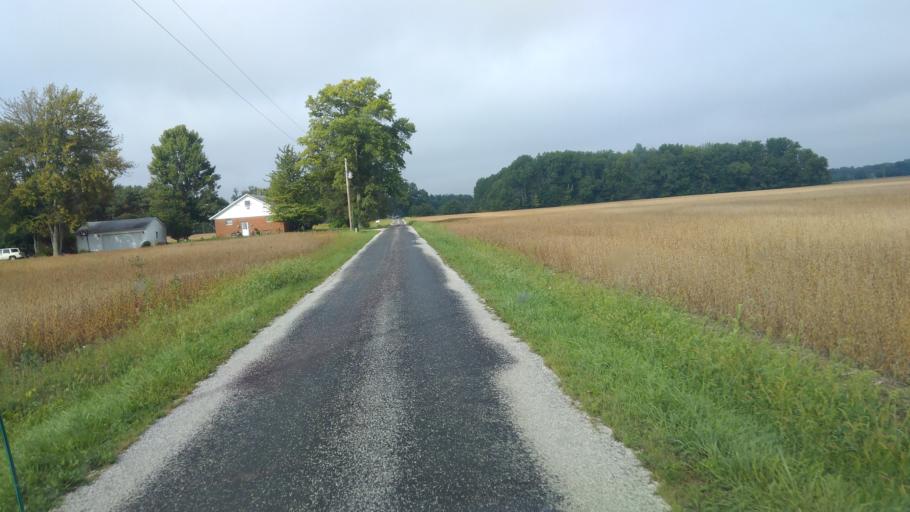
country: US
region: Ohio
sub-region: Morrow County
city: Cardington
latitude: 40.5504
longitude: -82.9864
